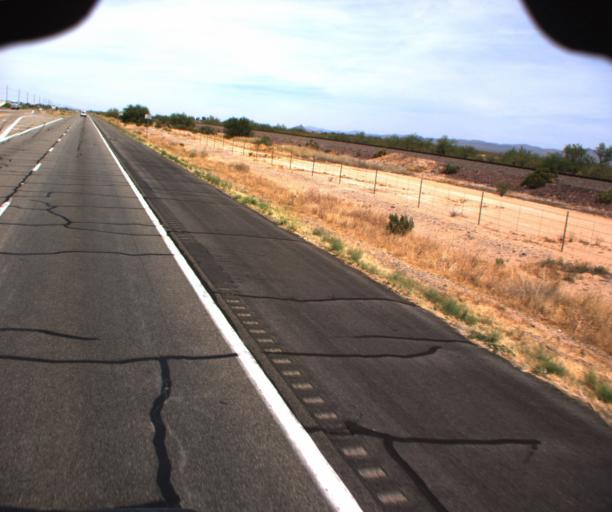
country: US
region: Arizona
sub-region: Maricopa County
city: Sun City West
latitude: 33.7609
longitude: -112.5067
